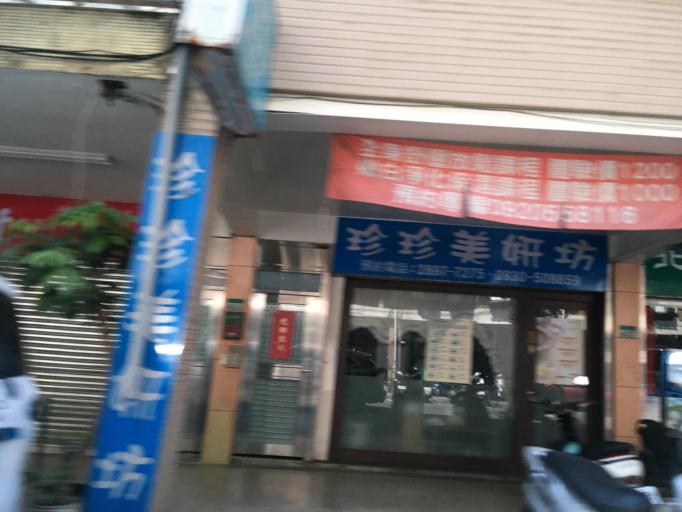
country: TW
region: Taipei
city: Taipei
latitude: 25.1439
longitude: 121.4979
